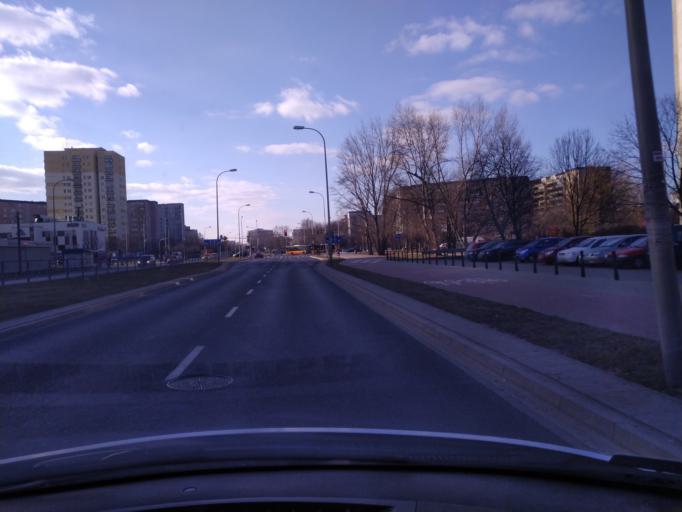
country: PL
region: Masovian Voivodeship
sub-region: Warszawa
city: Praga Poludnie
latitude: 52.2247
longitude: 21.0947
